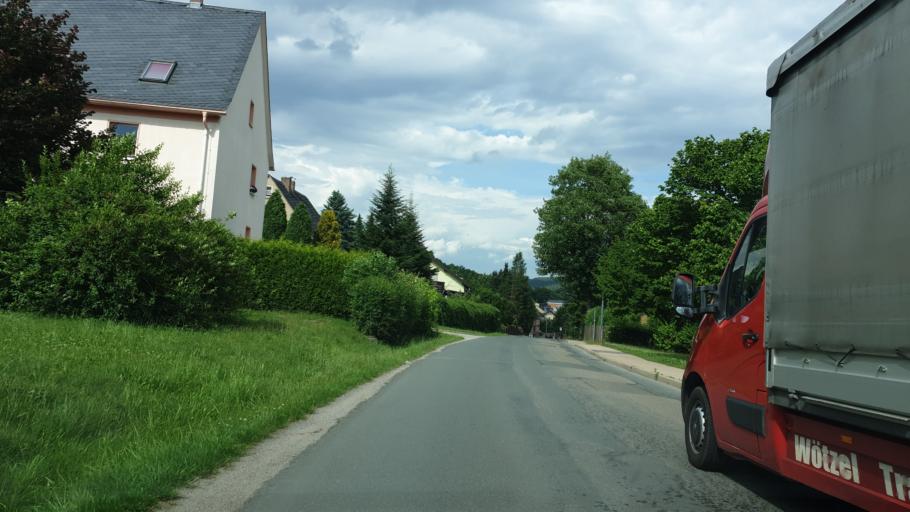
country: DE
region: Saxony
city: Lossnitz
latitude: 50.6192
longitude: 12.7237
